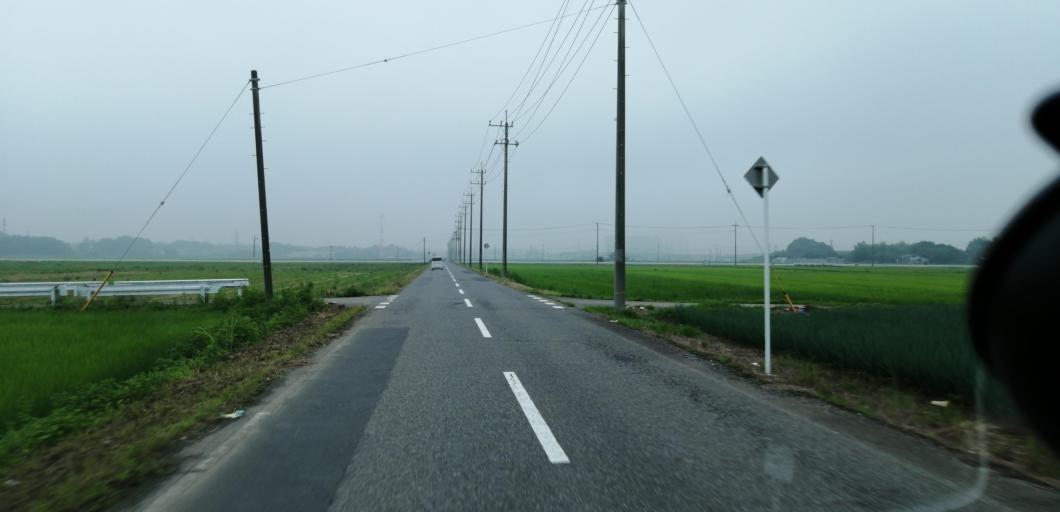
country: JP
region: Chiba
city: Noda
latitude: 35.9718
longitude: 139.9016
